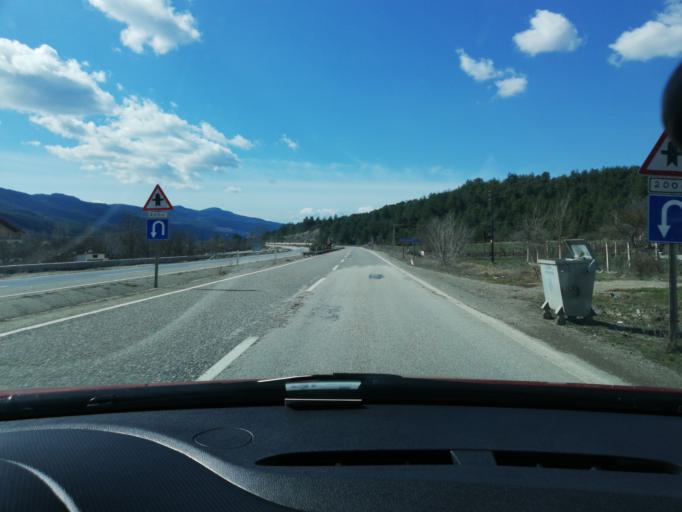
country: TR
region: Karabuk
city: Ovacik
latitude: 41.2045
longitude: 32.8870
